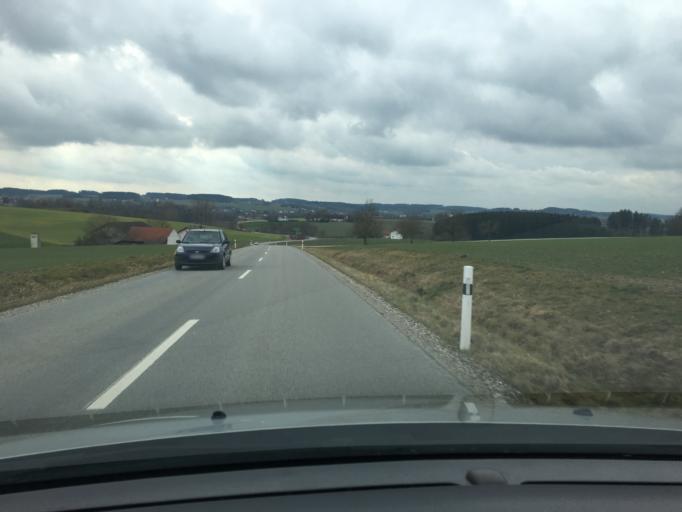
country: DE
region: Bavaria
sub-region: Lower Bavaria
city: Gangkofen
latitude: 48.4466
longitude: 12.5888
